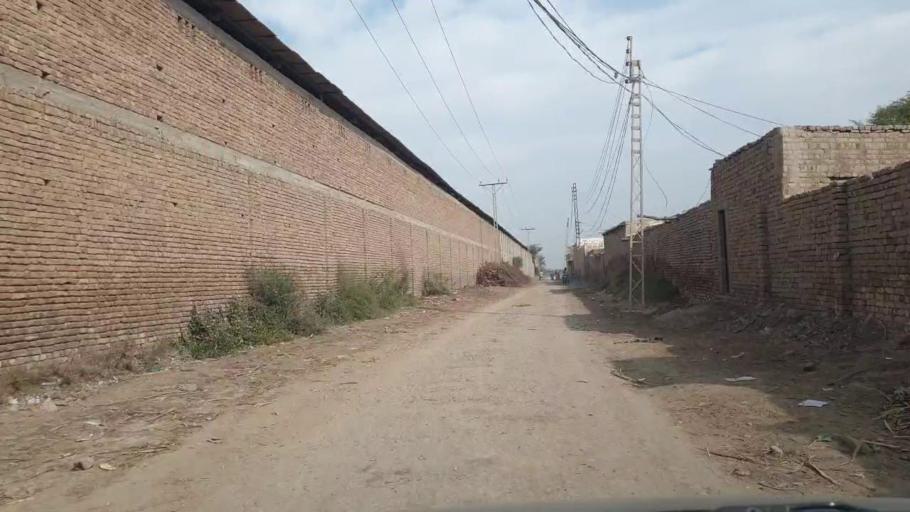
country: PK
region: Sindh
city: Shahdadpur
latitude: 25.9313
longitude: 68.6806
